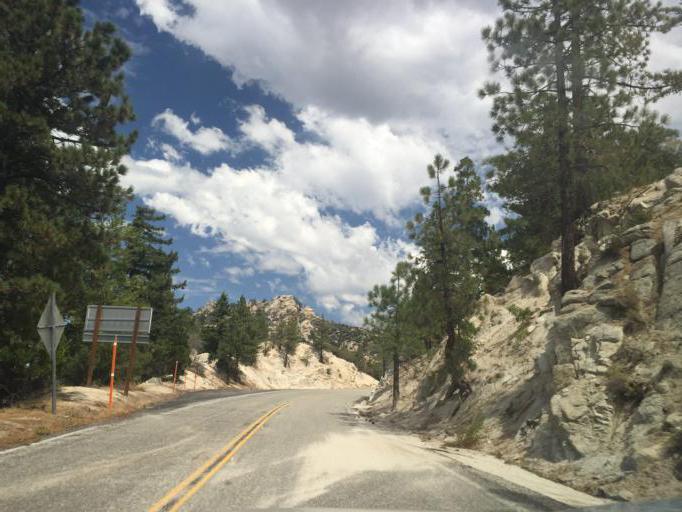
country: US
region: California
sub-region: Los Angeles County
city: Littlerock
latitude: 34.3432
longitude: -117.9802
